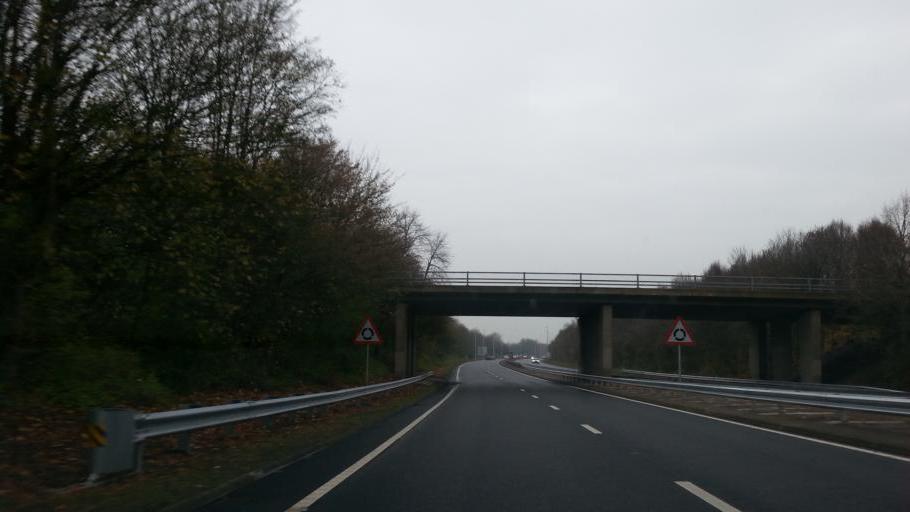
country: GB
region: England
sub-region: Cambridgeshire
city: Yaxley
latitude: 52.5411
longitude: -0.3046
